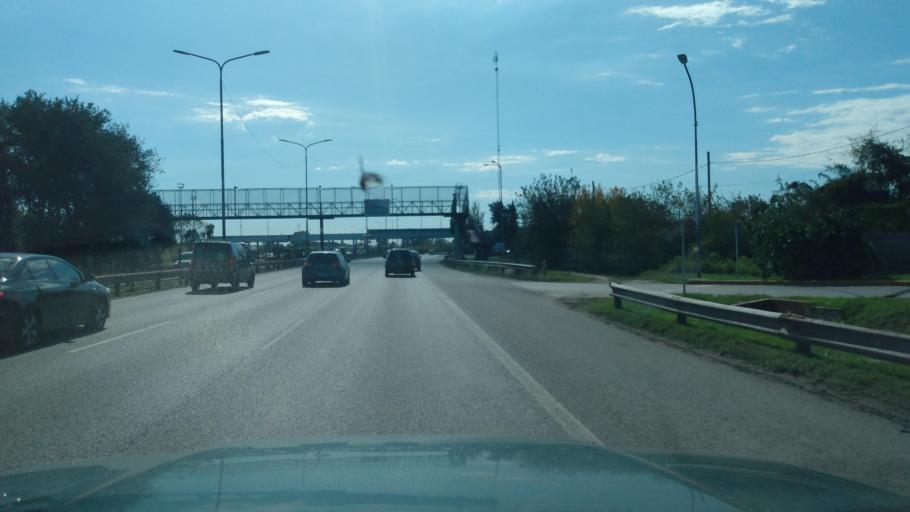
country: AR
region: Buenos Aires
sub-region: Partido de Tigre
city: Tigre
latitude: -34.5055
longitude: -58.5896
